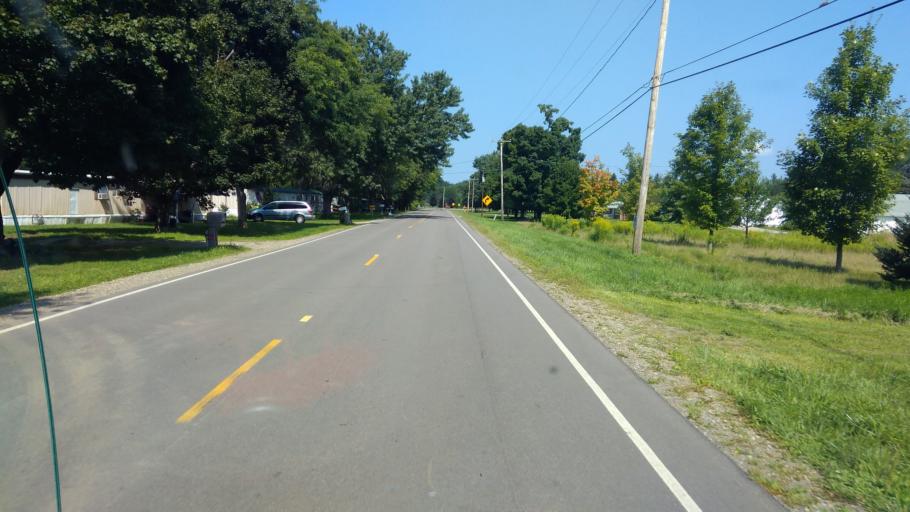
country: US
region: New York
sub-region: Allegany County
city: Belmont
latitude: 42.2354
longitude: -78.0388
